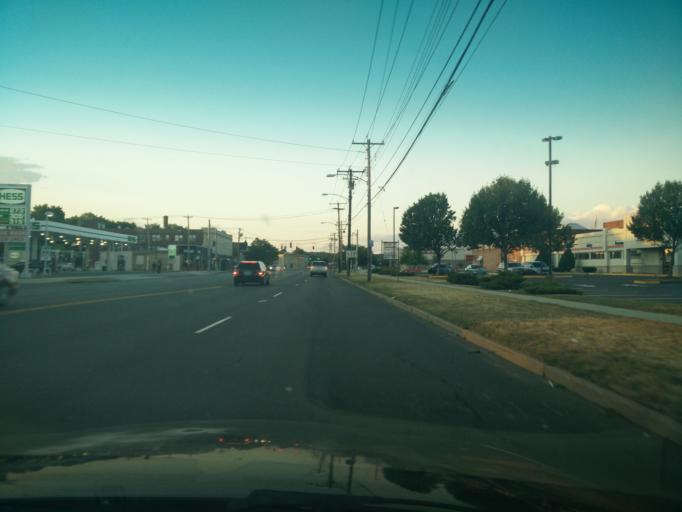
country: US
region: Connecticut
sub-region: New Haven County
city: New Haven
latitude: 41.3435
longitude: -72.9345
